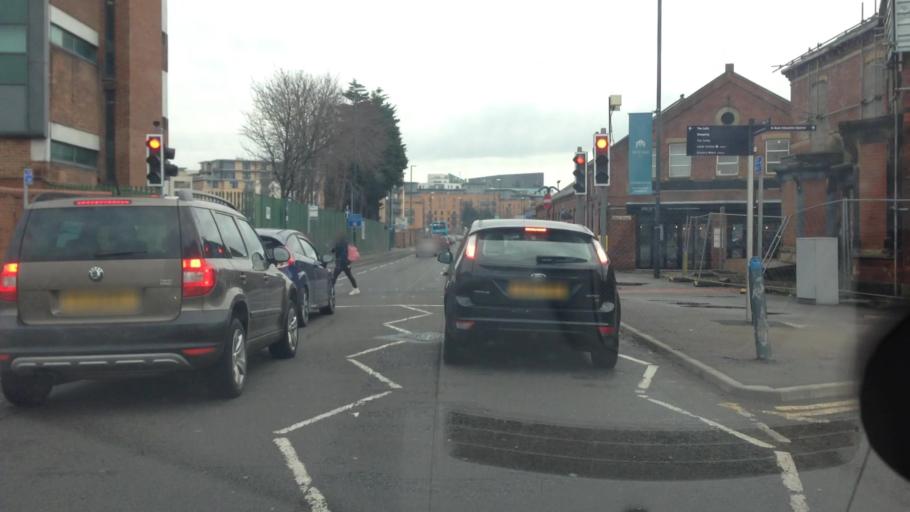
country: GB
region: England
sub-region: City and Borough of Leeds
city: Leeds
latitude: 53.7911
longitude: -1.5389
